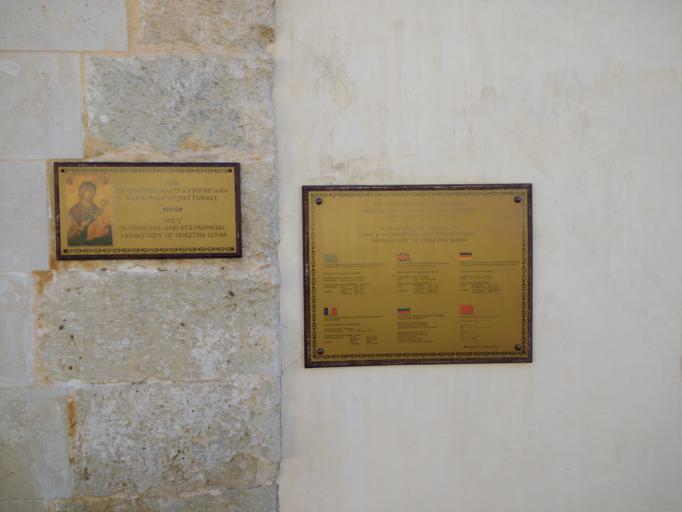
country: GR
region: Crete
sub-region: Nomos Chanias
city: Kolympari
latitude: 35.5506
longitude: 23.7767
